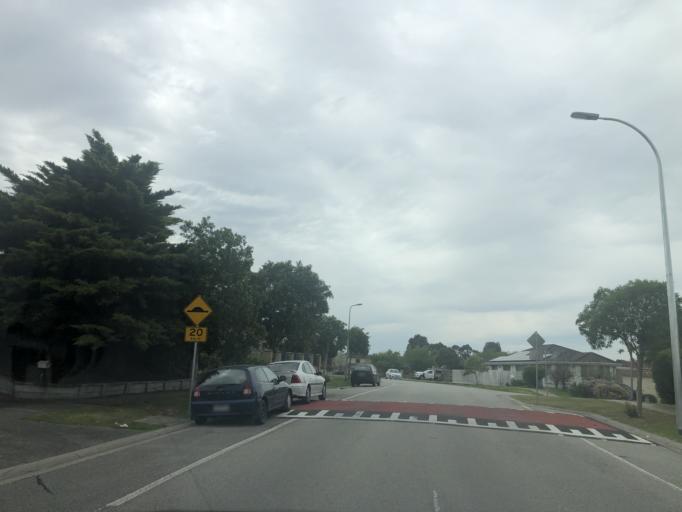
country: AU
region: Victoria
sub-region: Casey
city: Hallam
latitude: -38.0044
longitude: 145.2864
